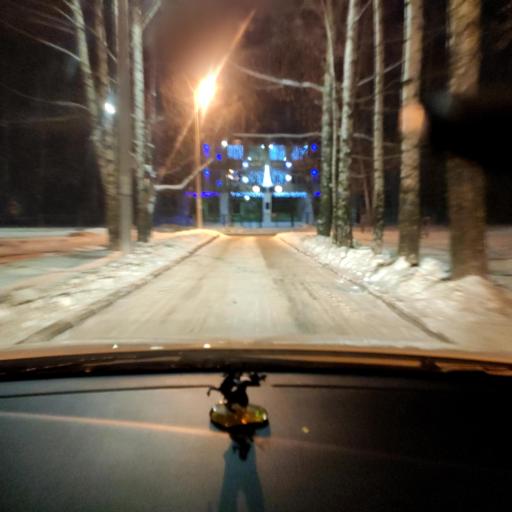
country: RU
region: Tatarstan
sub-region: Zelenodol'skiy Rayon
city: Zelenodolsk
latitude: 55.8513
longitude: 48.5598
